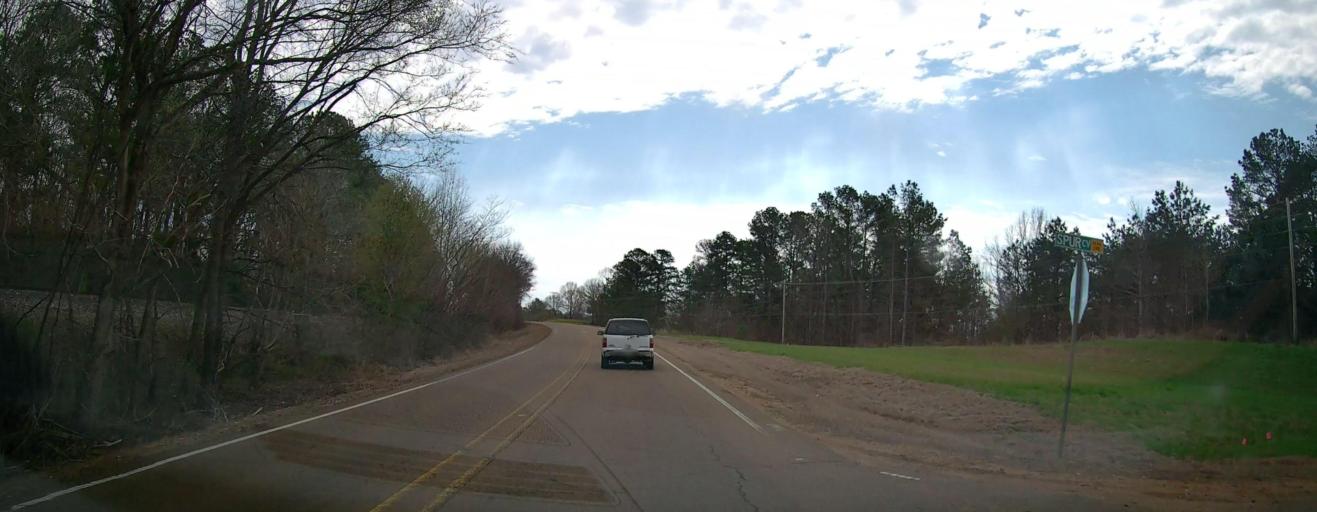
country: US
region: Mississippi
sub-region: Marshall County
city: Byhalia
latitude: 34.8895
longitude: -89.7310
